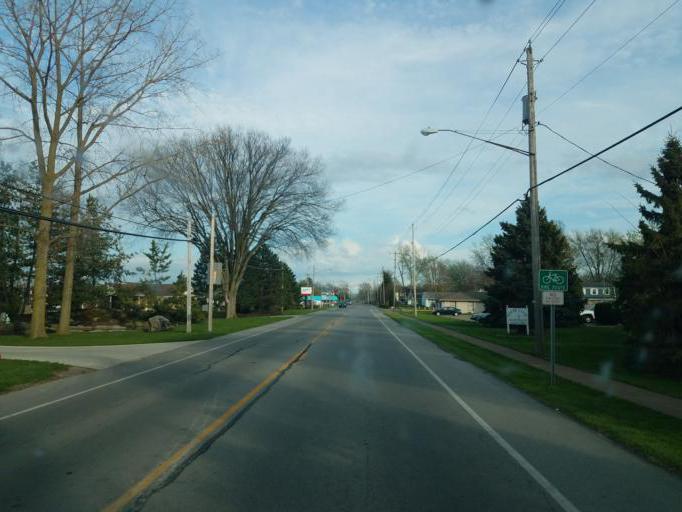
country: US
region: Ohio
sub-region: Erie County
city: Huron
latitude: 41.3990
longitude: -82.5621
